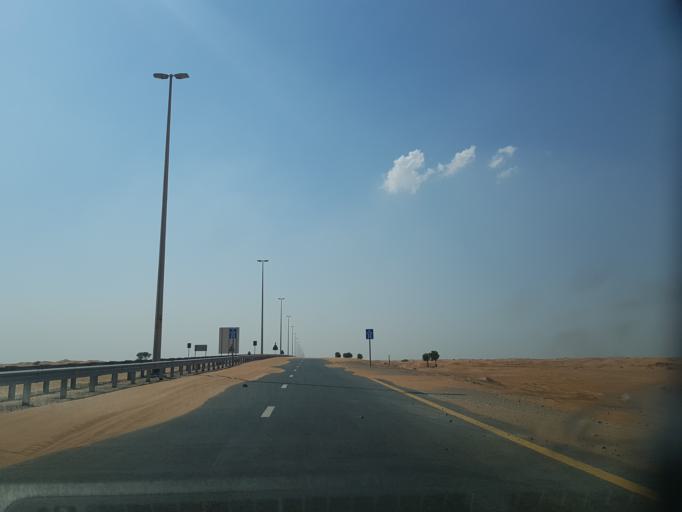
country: AE
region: Ash Shariqah
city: Adh Dhayd
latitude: 25.2557
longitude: 55.7331
